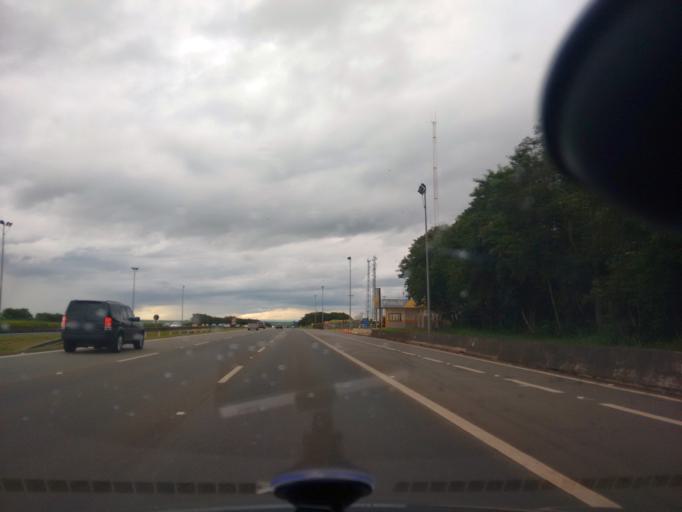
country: BR
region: Sao Paulo
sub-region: Santa Barbara D'Oeste
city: Santa Barbara d'Oeste
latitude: -22.8125
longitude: -47.3876
